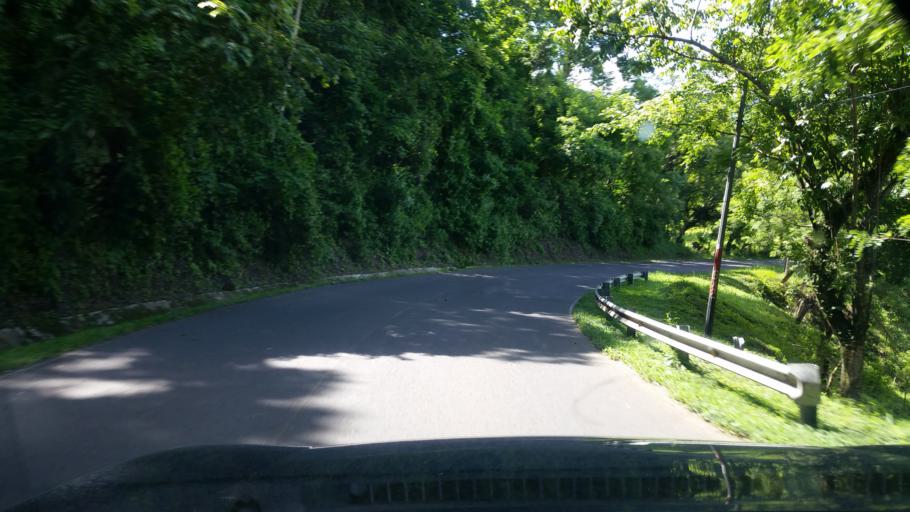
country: NI
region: Matagalpa
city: San Ramon
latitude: 13.0161
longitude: -85.7901
